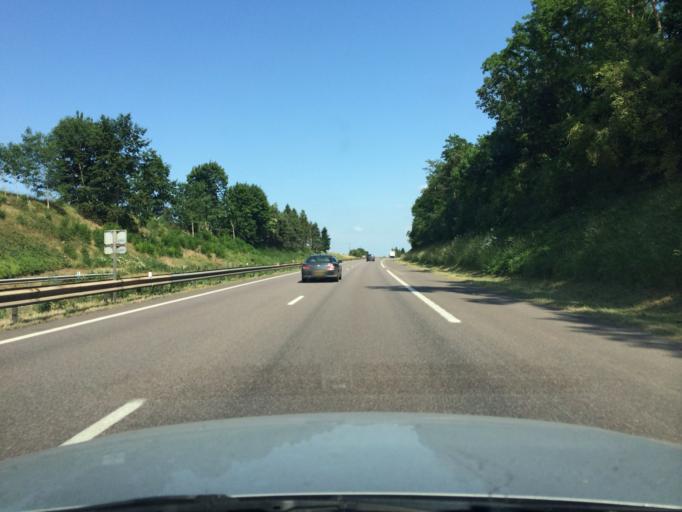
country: FR
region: Alsace
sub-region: Departement du Bas-Rhin
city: Mommenheim
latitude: 48.7710
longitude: 7.6281
